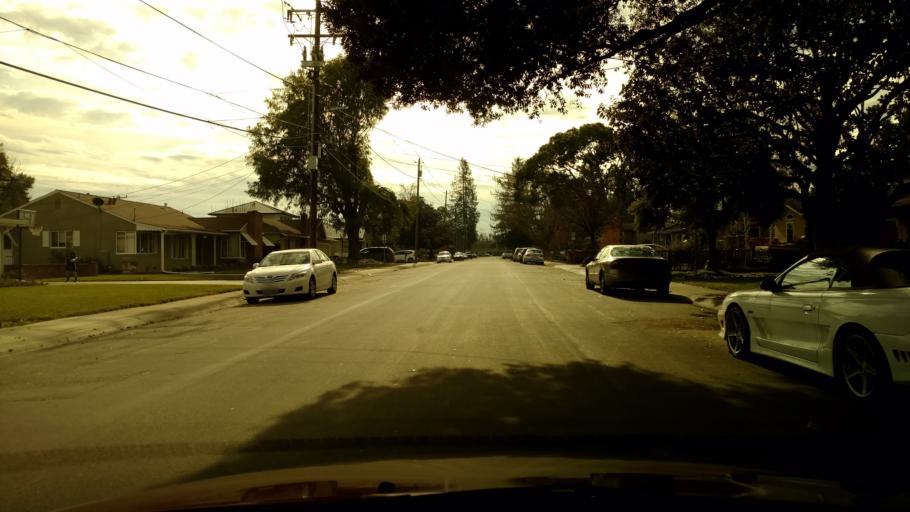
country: US
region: California
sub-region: Santa Clara County
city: Buena Vista
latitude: 37.2972
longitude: -121.9210
